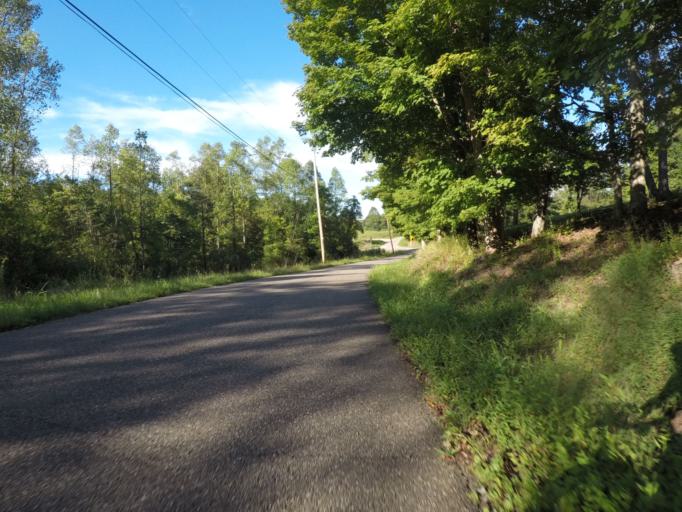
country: US
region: West Virginia
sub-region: Cabell County
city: Huntington
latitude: 38.4725
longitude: -82.4595
